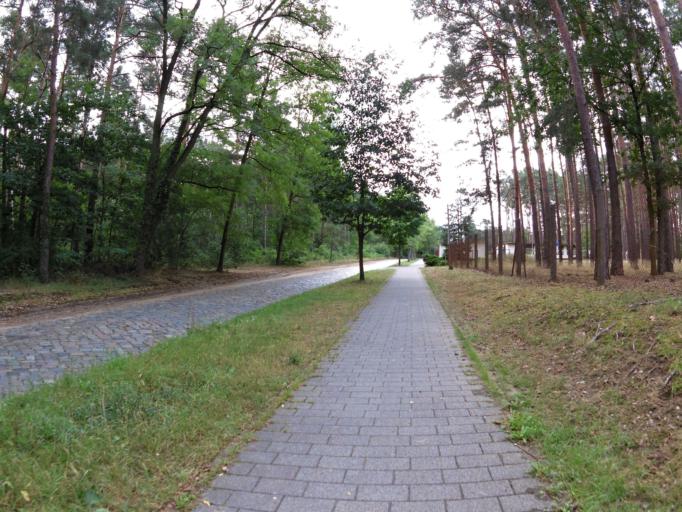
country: DE
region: Brandenburg
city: Storkow
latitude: 52.2615
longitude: 13.9597
